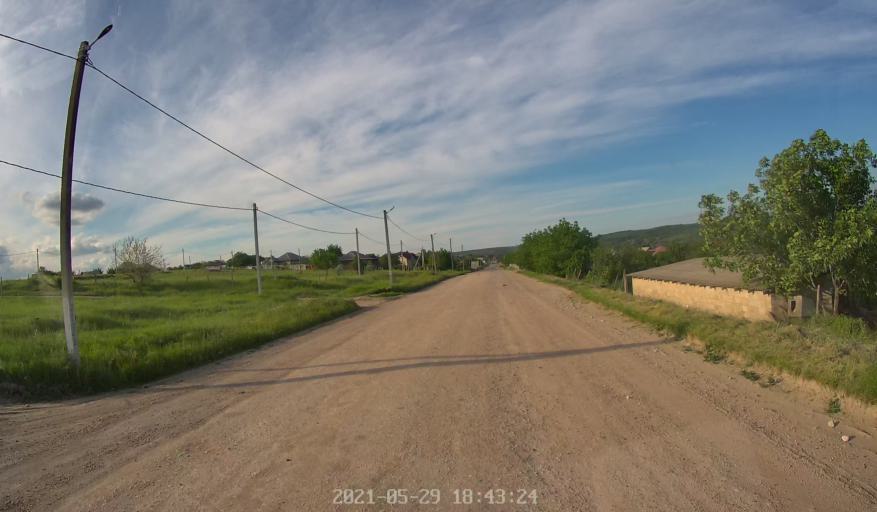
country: MD
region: Chisinau
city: Singera
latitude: 46.8184
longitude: 28.9646
